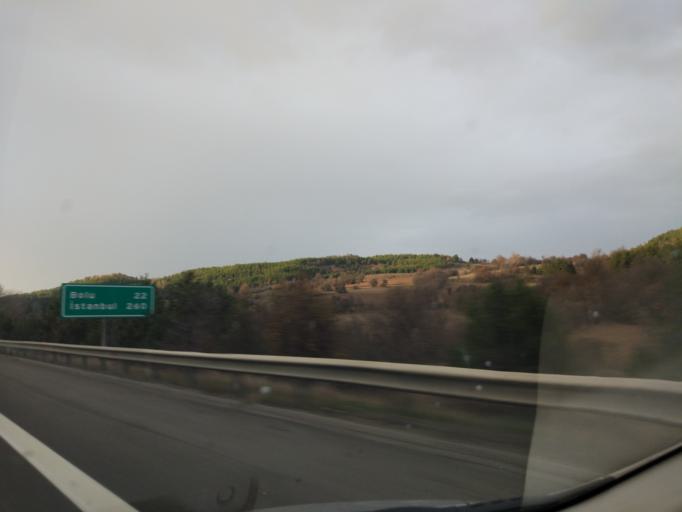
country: TR
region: Bolu
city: Bolu
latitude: 40.7377
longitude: 31.7967
